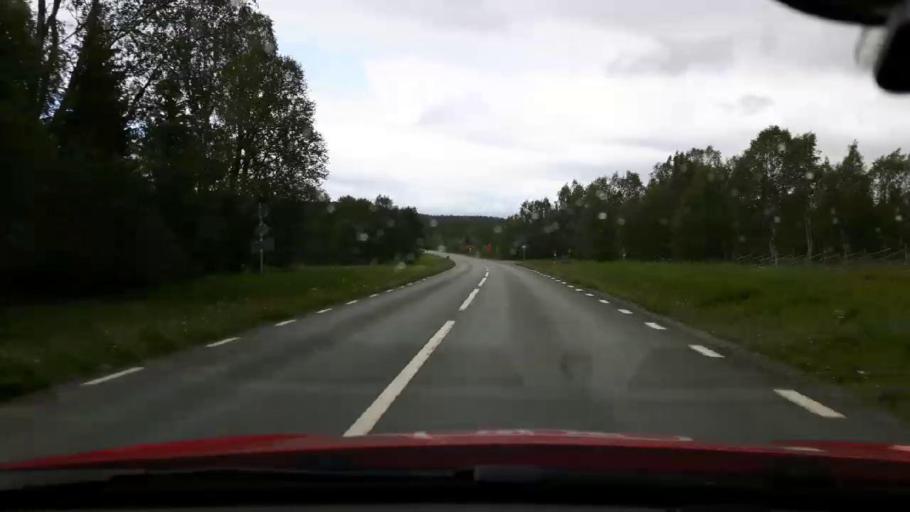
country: SE
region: Jaemtland
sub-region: Are Kommun
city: Are
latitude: 63.3634
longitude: 12.6984
